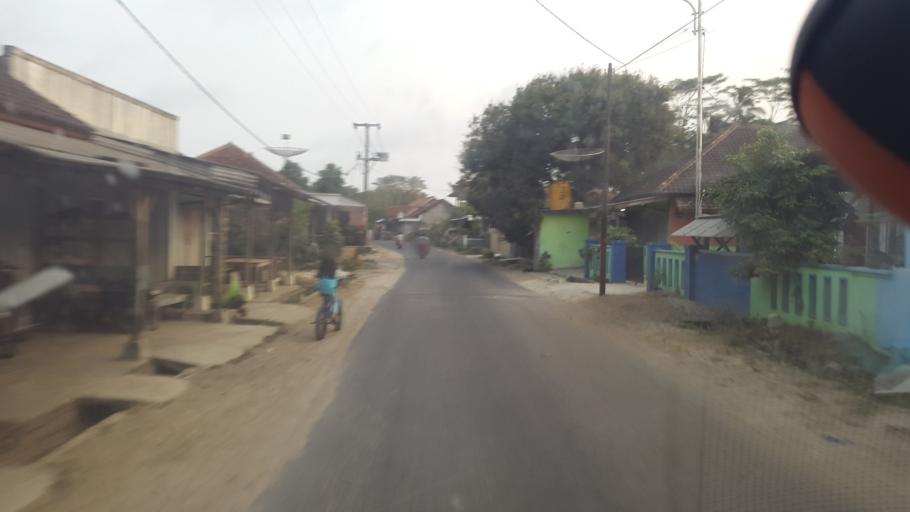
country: ID
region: West Java
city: Cibungur
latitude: -7.3718
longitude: 106.5384
